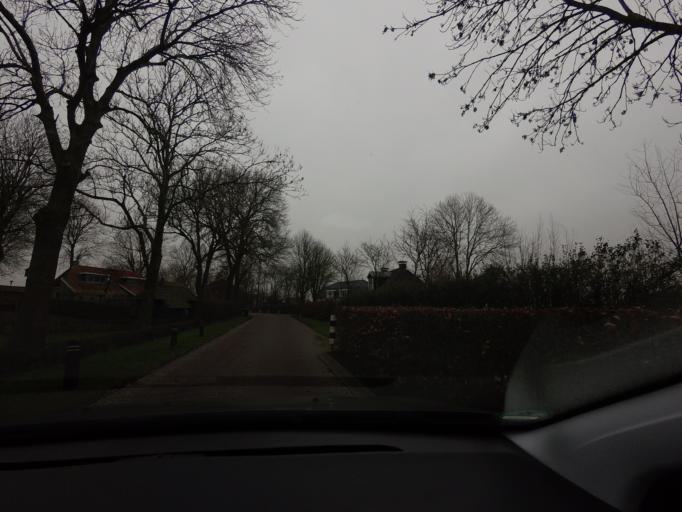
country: NL
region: Friesland
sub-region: Sudwest Fryslan
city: Bolsward
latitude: 53.1095
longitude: 5.5390
